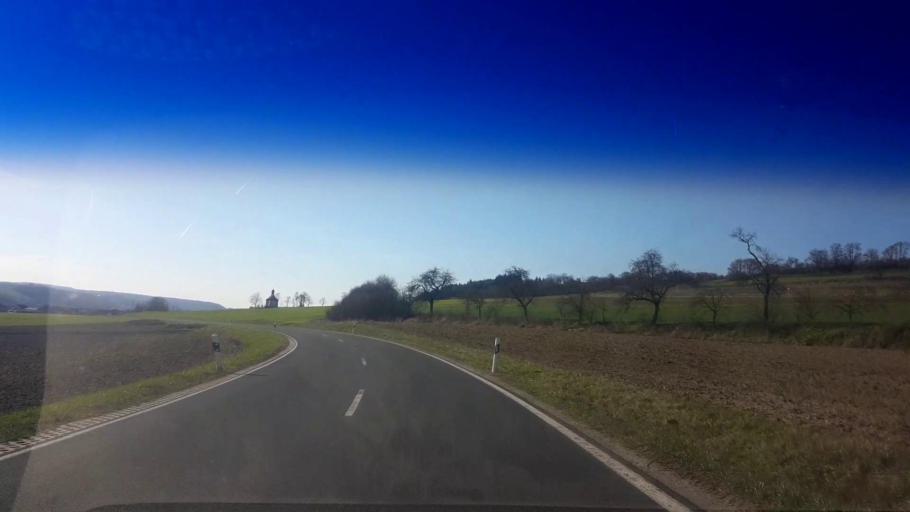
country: DE
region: Bavaria
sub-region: Regierungsbezirk Unterfranken
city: Stettfeld
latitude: 49.9682
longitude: 10.7424
